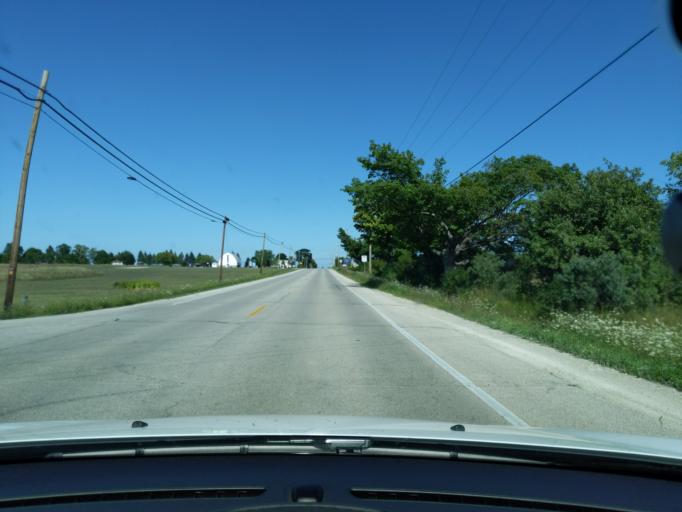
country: US
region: Michigan
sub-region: Delta County
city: Escanaba
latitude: 45.2443
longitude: -87.0870
